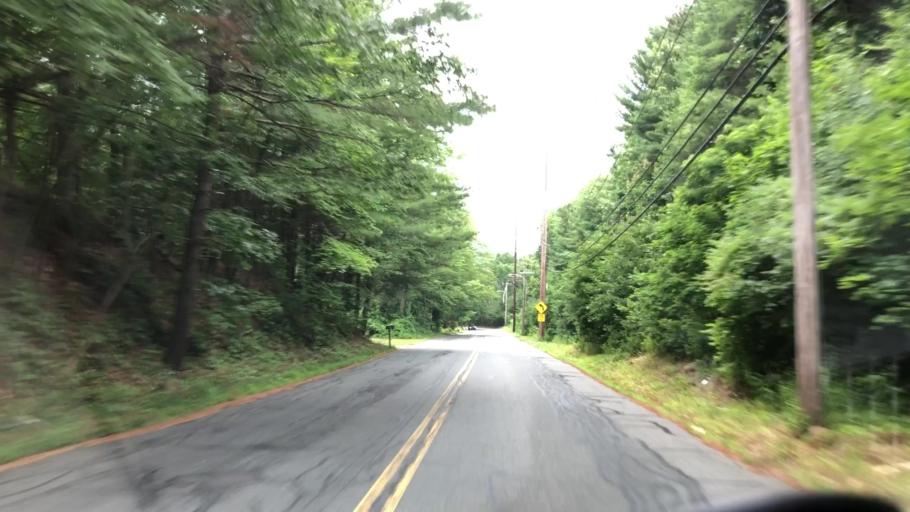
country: US
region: Massachusetts
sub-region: Hampden County
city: Holyoke
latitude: 42.1902
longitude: -72.6700
